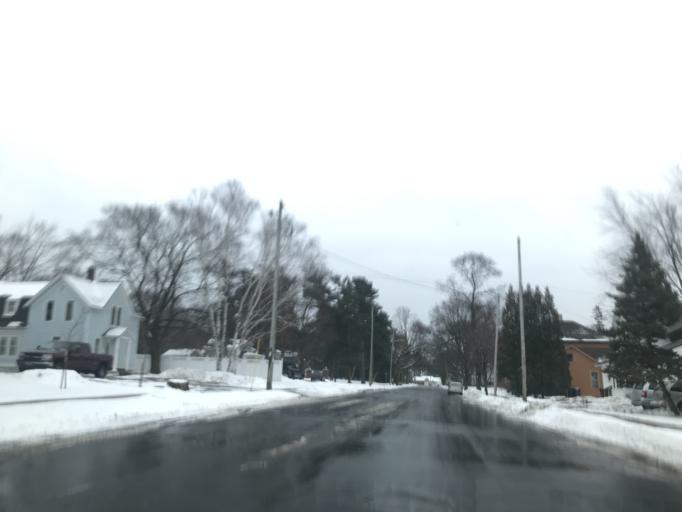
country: US
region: Wisconsin
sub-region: Door County
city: Sturgeon Bay
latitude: 44.8389
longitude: -87.3738
